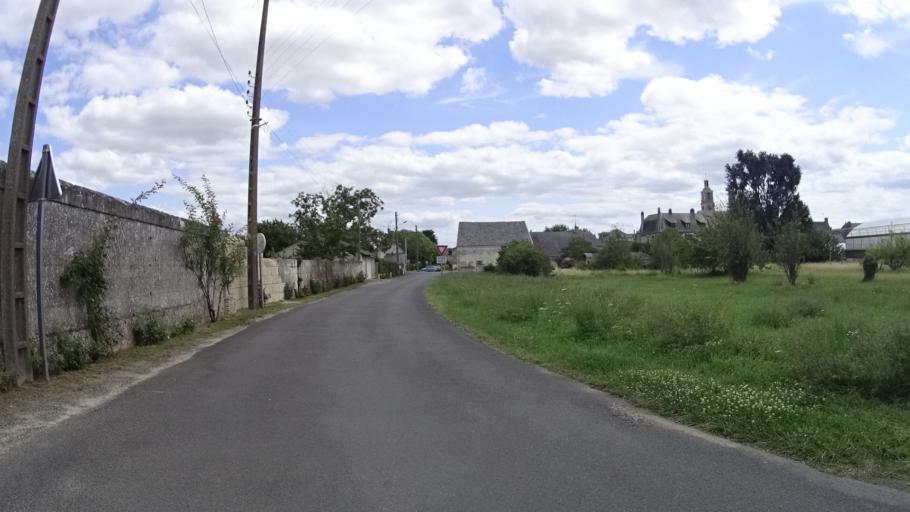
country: FR
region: Pays de la Loire
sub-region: Departement de Maine-et-Loire
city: La Menitre
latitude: 47.4037
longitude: -0.2722
